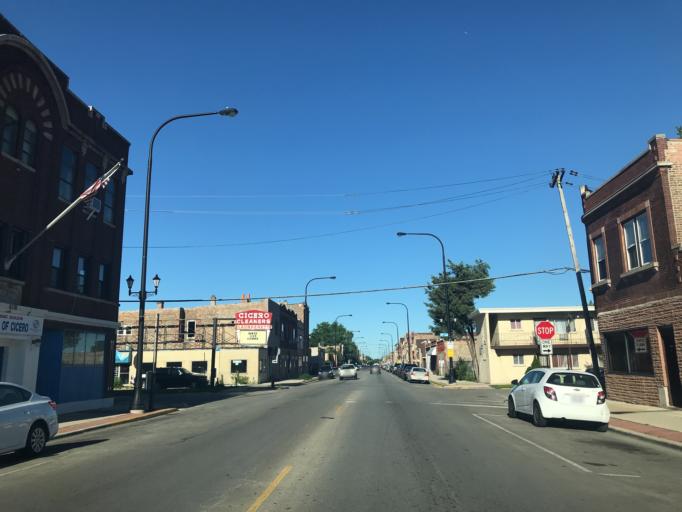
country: US
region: Illinois
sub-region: Cook County
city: Cicero
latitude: 41.8456
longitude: -87.7618
